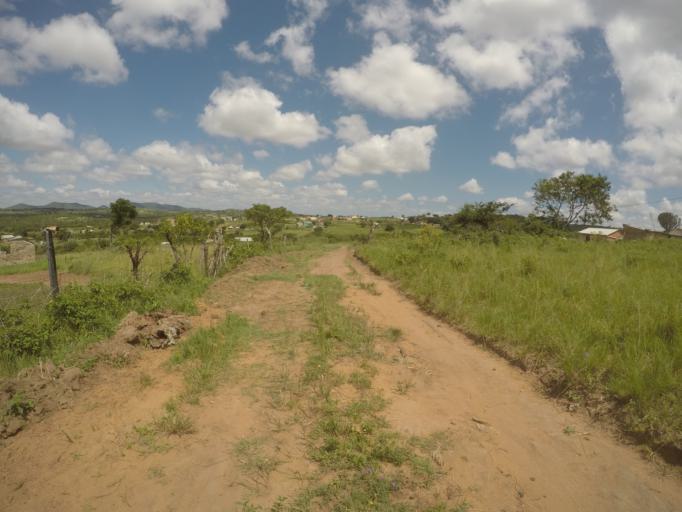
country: ZA
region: KwaZulu-Natal
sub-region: uThungulu District Municipality
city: Empangeni
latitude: -28.5817
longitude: 31.8411
